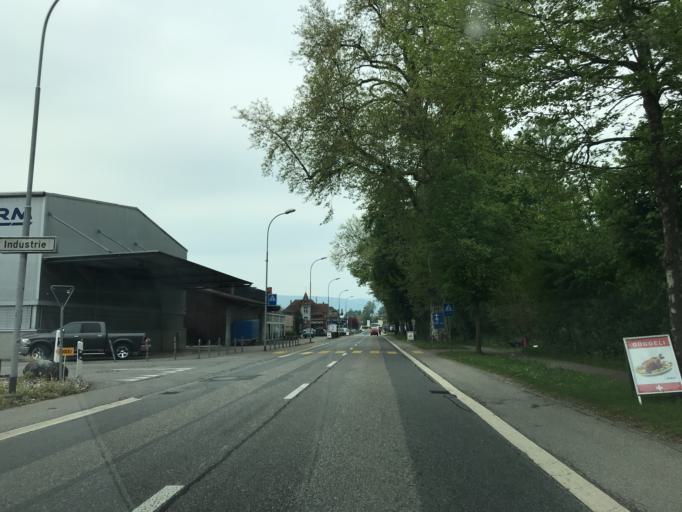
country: CH
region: Bern
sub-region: Oberaargau
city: Aarwangen
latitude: 47.2302
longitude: 7.7760
